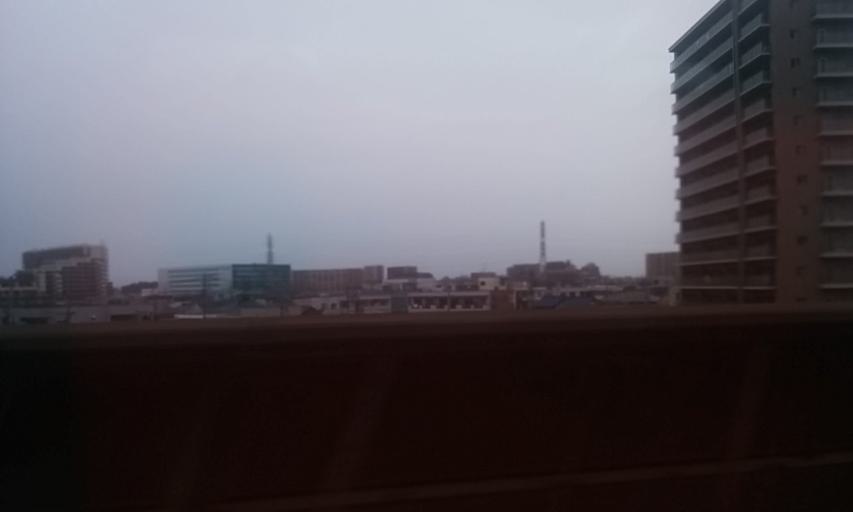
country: JP
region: Saitama
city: Ageoshimo
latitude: 35.9349
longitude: 139.6167
